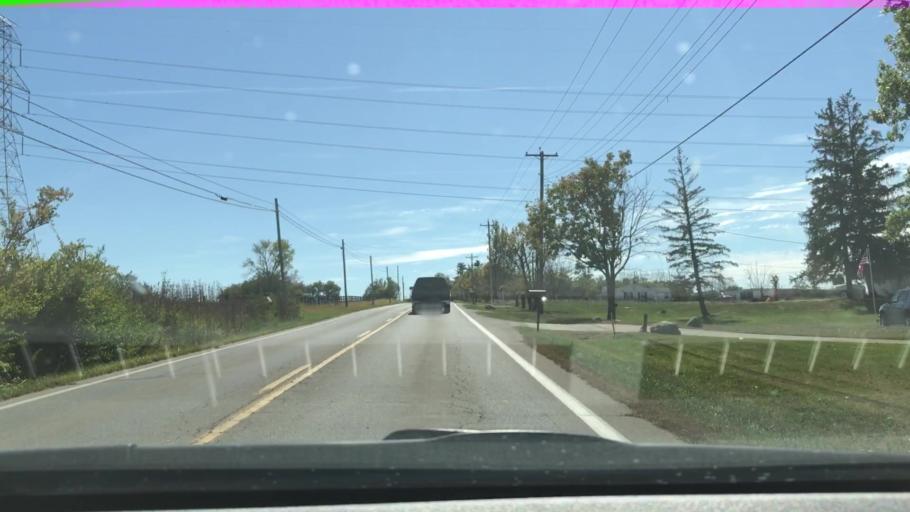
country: US
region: Ohio
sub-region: Butler County
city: Hamilton
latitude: 39.4500
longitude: -84.6203
